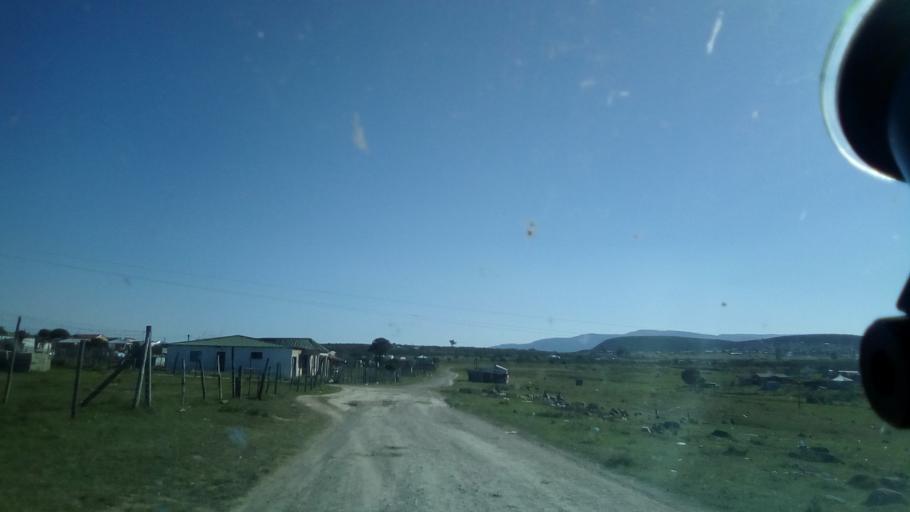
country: ZA
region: Eastern Cape
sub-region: Buffalo City Metropolitan Municipality
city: Bhisho
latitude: -32.8308
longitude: 27.3716
